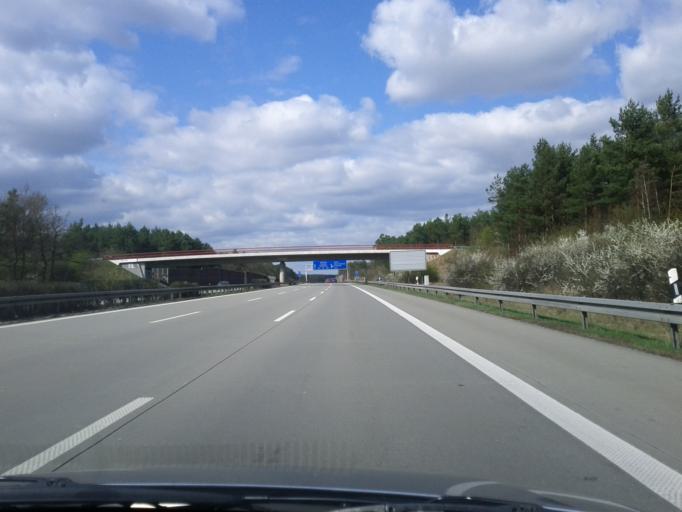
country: DE
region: Brandenburg
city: Grunheide
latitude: 52.4116
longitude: 13.7845
